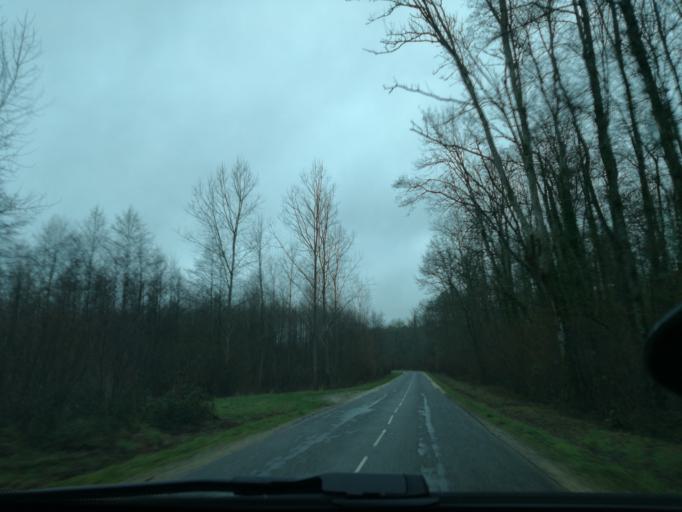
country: FR
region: Lorraine
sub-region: Departement de la Meuse
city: Clermont-en-Argonne
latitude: 49.0387
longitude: 5.1201
